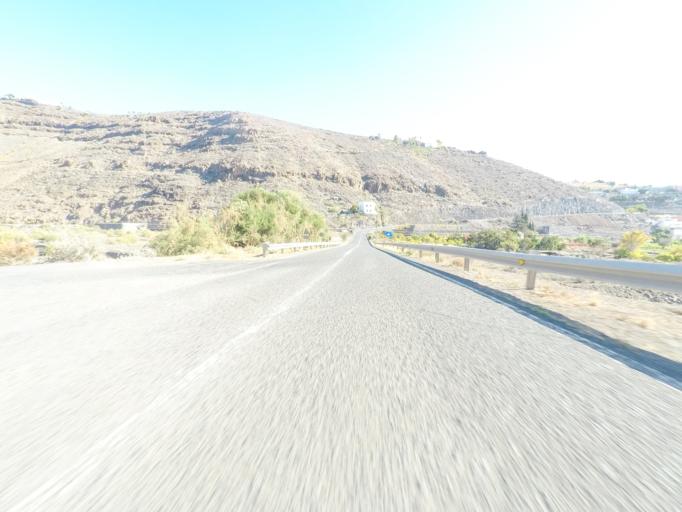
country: ES
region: Canary Islands
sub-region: Provincia de Santa Cruz de Tenerife
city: Alajero
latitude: 28.0337
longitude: -17.1984
